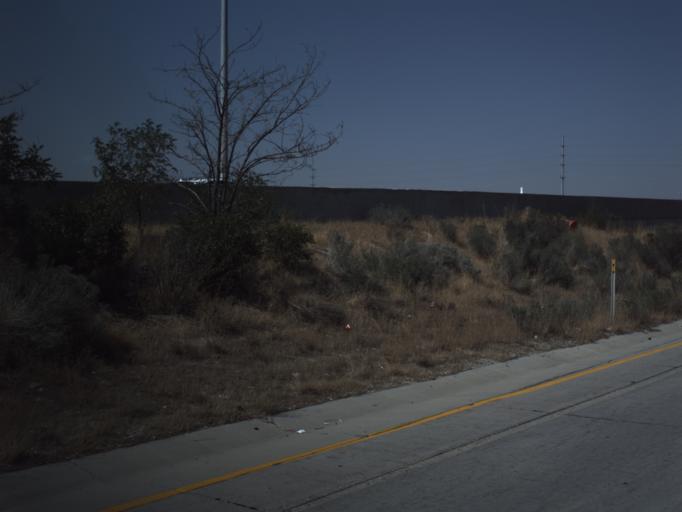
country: US
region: Utah
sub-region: Salt Lake County
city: Sandy City
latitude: 40.5857
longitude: -111.8996
